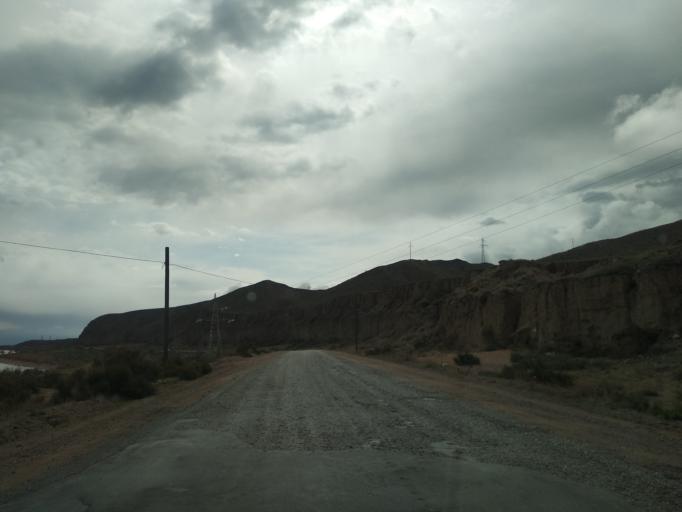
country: KG
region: Ysyk-Koel
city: Kadzhi-Say
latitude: 42.1790
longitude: 77.2951
